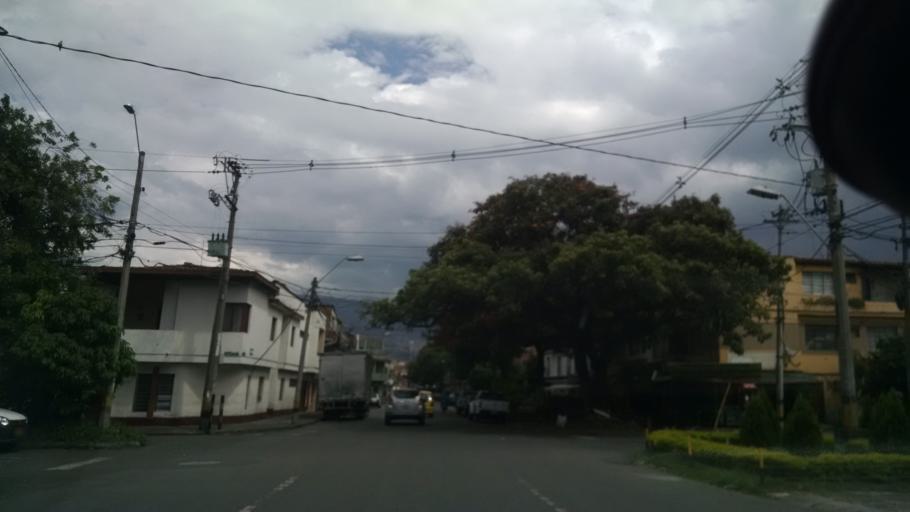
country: CO
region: Antioquia
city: Medellin
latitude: 6.2480
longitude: -75.5851
